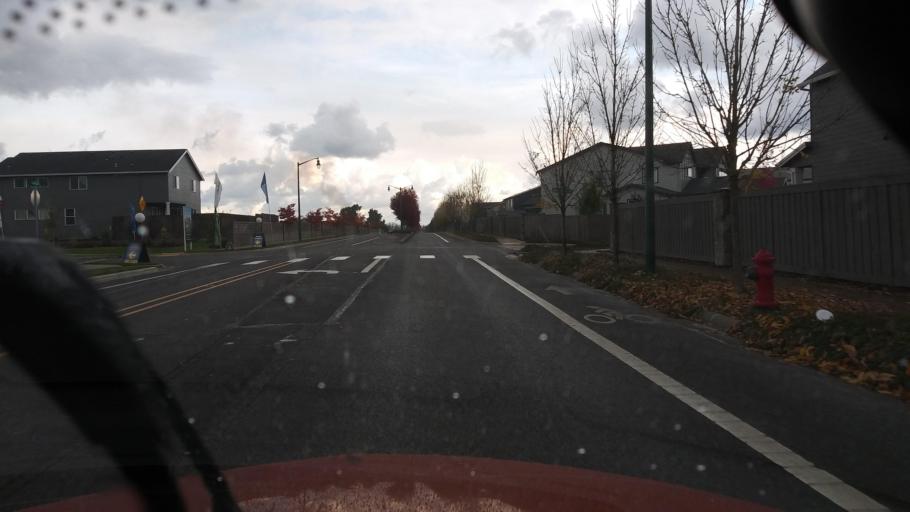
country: US
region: Oregon
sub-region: Washington County
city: Forest Grove
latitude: 45.5392
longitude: -123.1206
